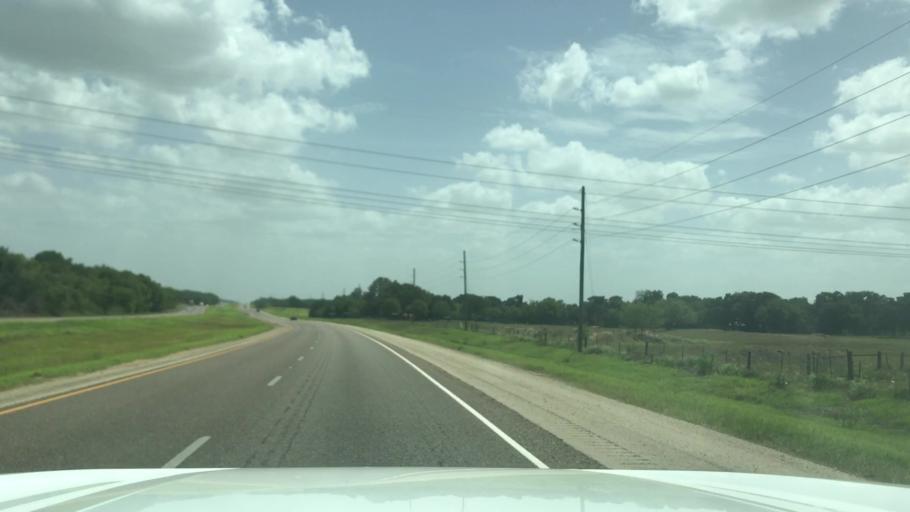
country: US
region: Texas
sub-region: Robertson County
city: Calvert
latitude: 31.0986
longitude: -96.7153
